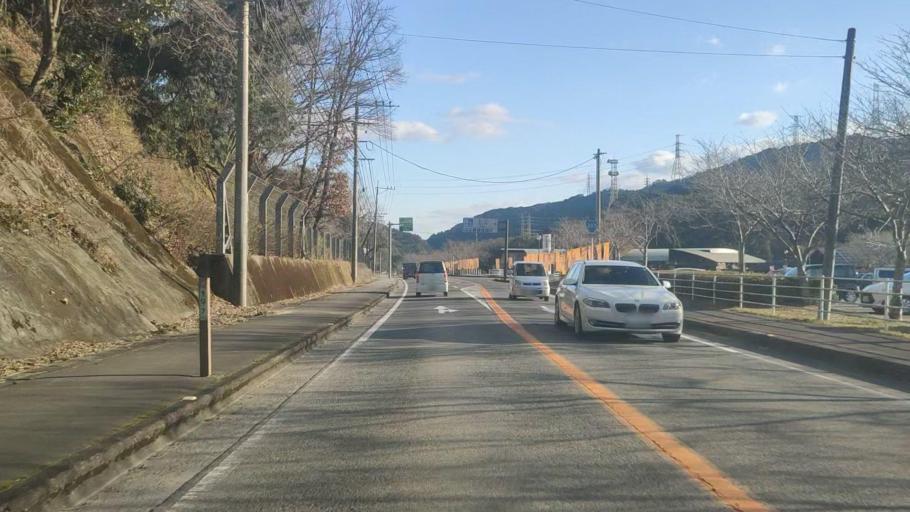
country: JP
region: Saga Prefecture
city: Saga-shi
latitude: 33.3405
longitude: 130.2571
